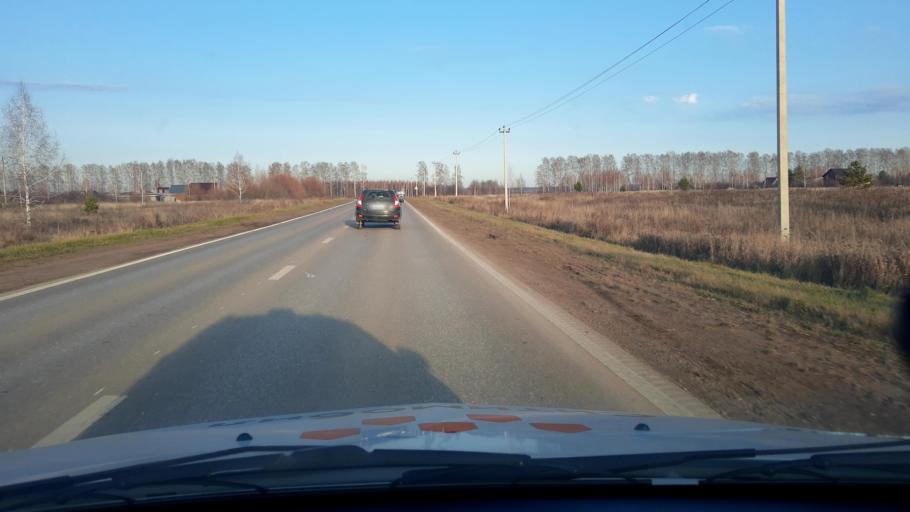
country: RU
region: Bashkortostan
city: Kabakovo
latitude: 54.7018
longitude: 56.1661
